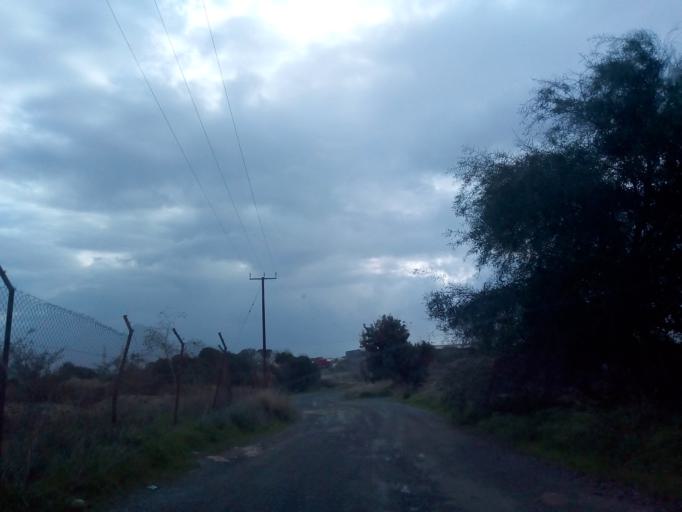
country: CY
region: Limassol
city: Ypsonas
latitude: 34.6775
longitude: 32.9732
